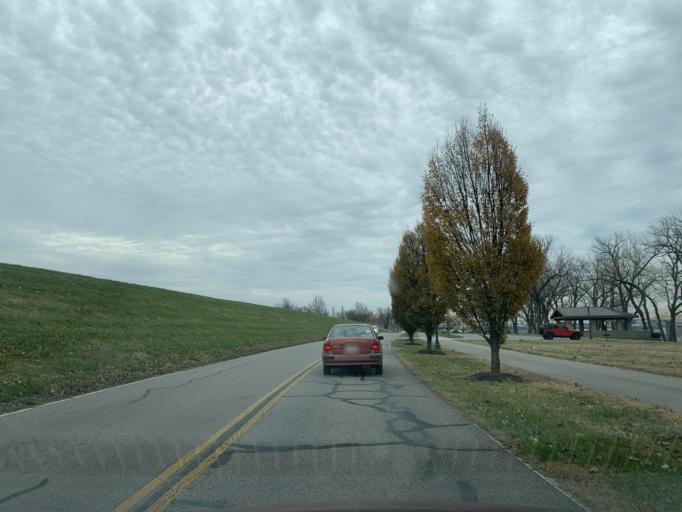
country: US
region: Kentucky
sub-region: Jefferson County
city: Louisville
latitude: 38.2726
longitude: -85.7581
